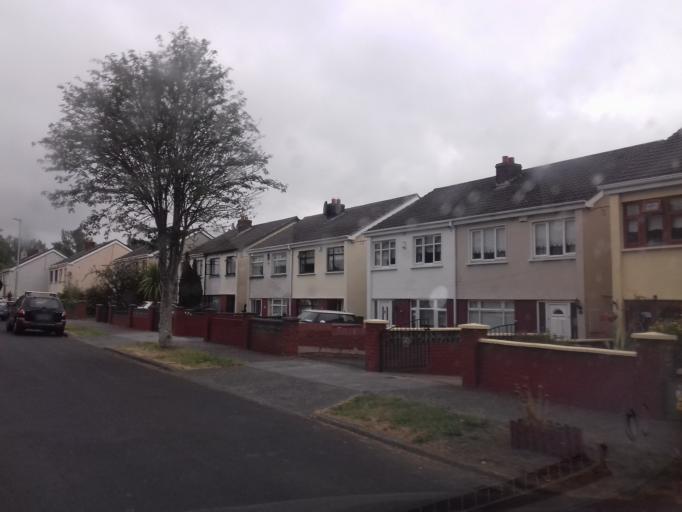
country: IE
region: Leinster
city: Hartstown
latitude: 53.3987
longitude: -6.4058
